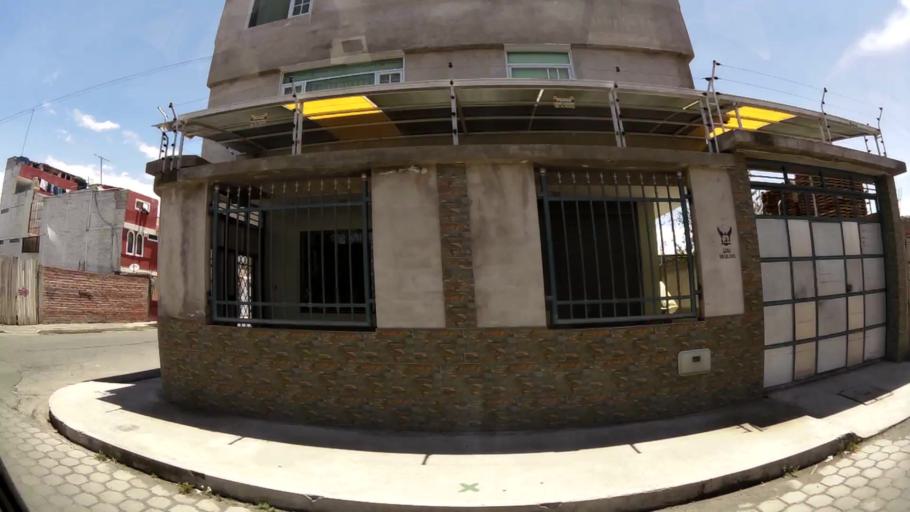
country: EC
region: Chimborazo
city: Riobamba
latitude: -1.6820
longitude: -78.6517
